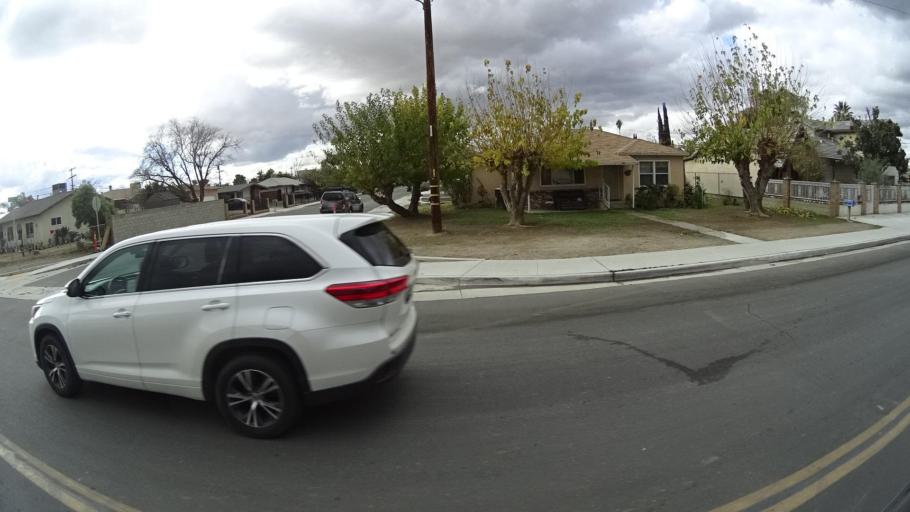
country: US
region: California
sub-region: Kern County
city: Greenfield
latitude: 35.3051
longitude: -118.9942
